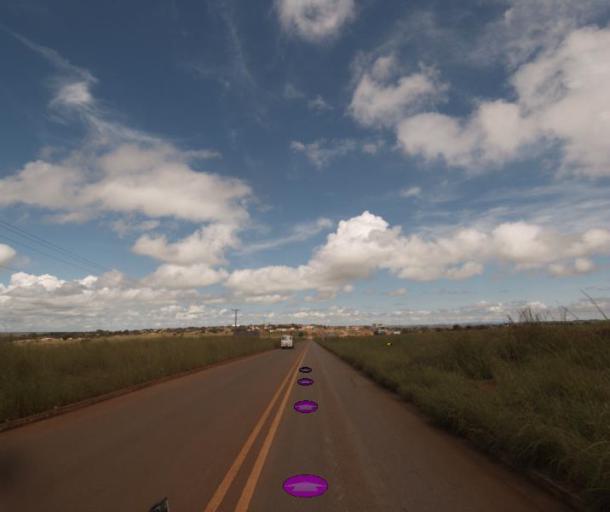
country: BR
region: Federal District
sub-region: Brasilia
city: Brasilia
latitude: -15.7458
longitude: -48.3188
